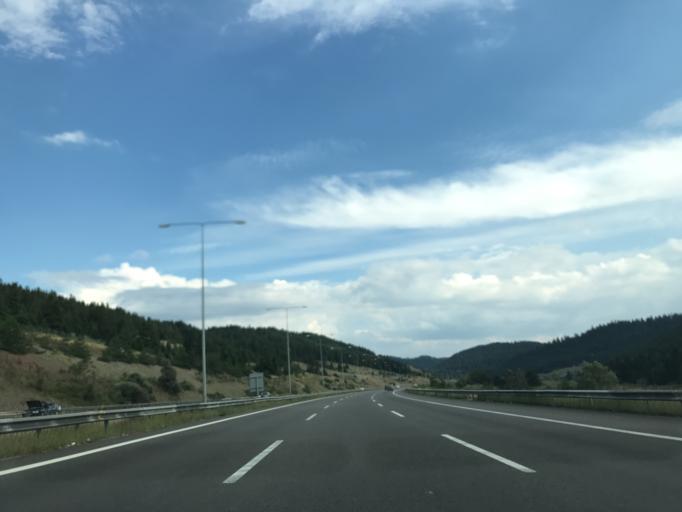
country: TR
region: Ankara
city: Pecenek
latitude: 40.6116
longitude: 32.2700
